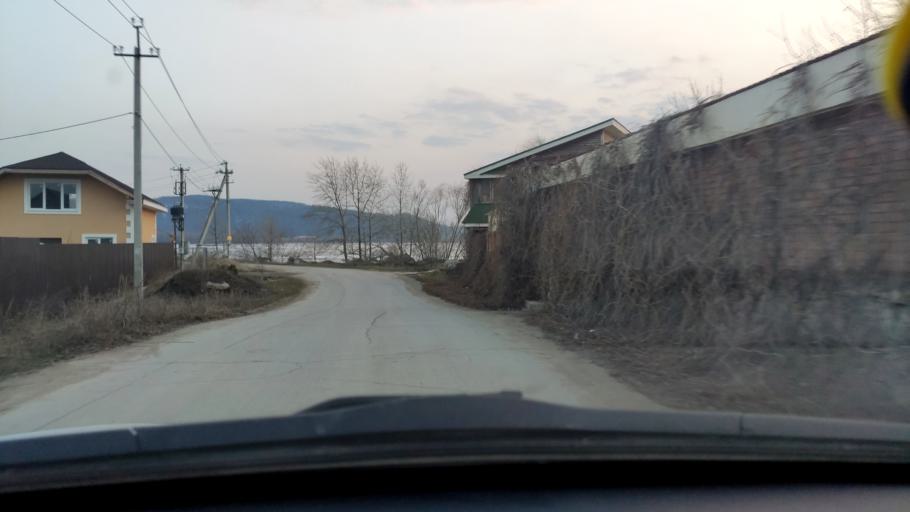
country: RU
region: Samara
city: Zhigulevsk
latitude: 53.4563
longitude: 49.5175
